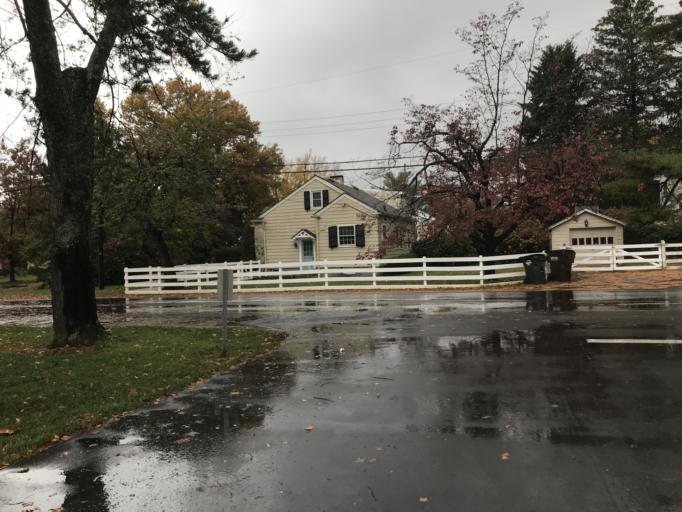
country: US
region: Kentucky
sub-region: Jefferson County
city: Saint Matthews
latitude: 38.2488
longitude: -85.6500
